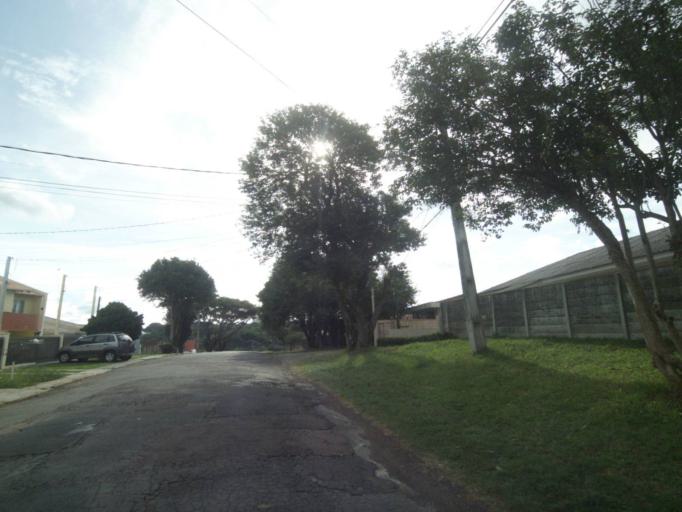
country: BR
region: Parana
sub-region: Curitiba
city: Curitiba
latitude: -25.4412
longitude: -49.3115
